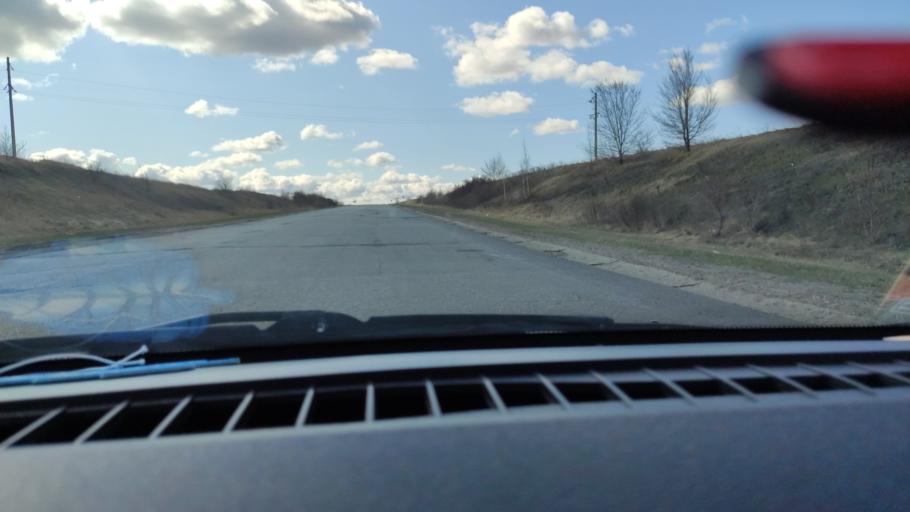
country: RU
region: Samara
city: Varlamovo
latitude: 53.0880
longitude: 48.3550
